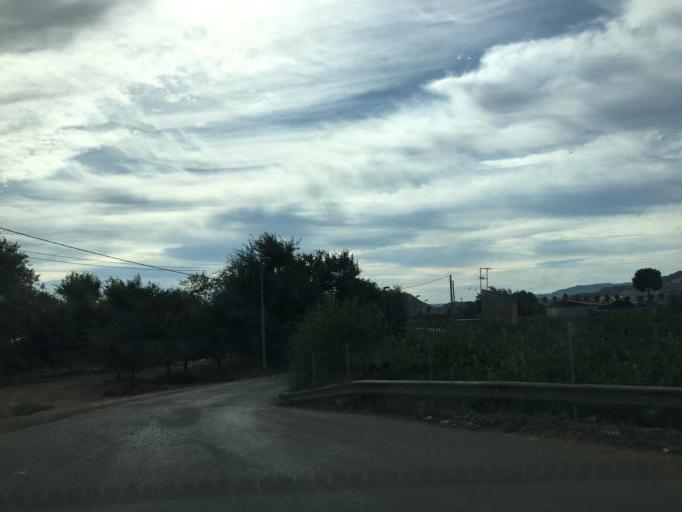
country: ES
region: Murcia
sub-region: Murcia
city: Santomera
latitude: 38.0124
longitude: -1.0436
